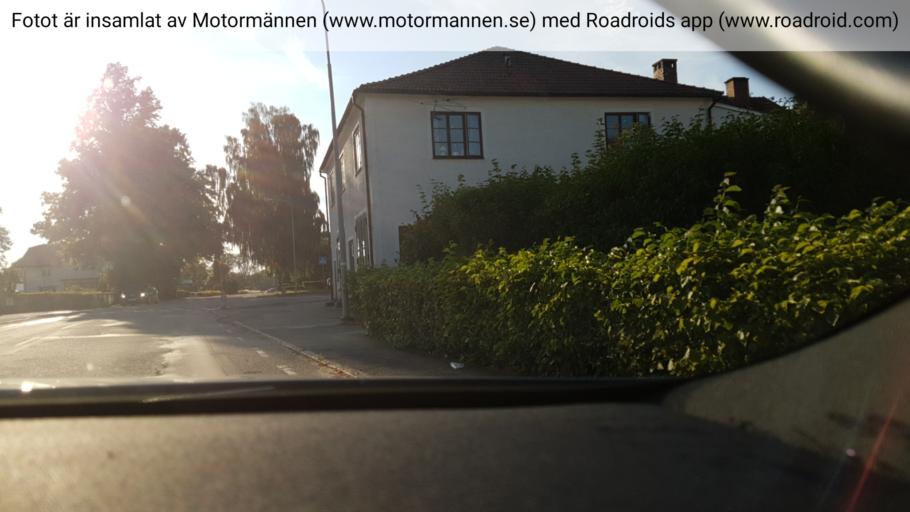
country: SE
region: Vaestra Goetaland
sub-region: Skara Kommun
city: Axvall
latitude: 58.3886
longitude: 13.5744
